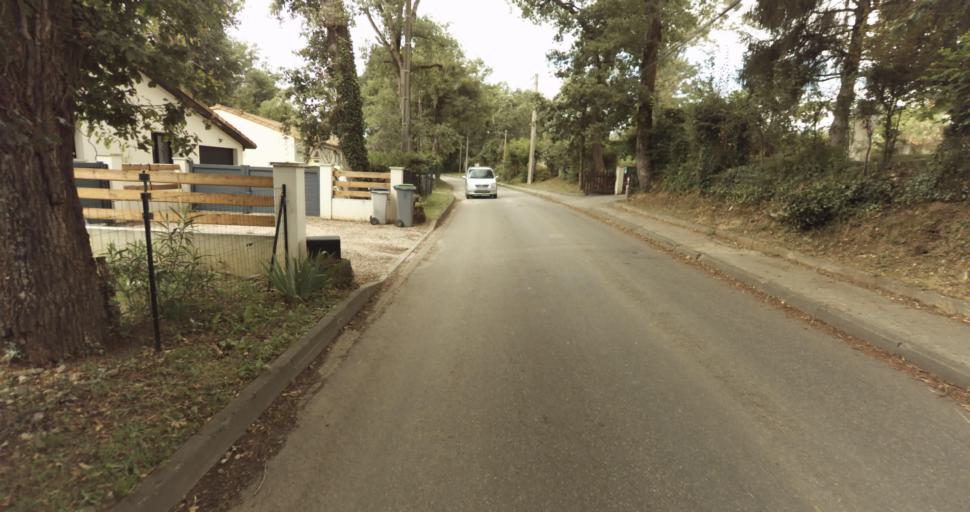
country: FR
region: Midi-Pyrenees
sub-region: Departement de la Haute-Garonne
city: Fontenilles
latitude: 43.5549
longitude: 1.1902
